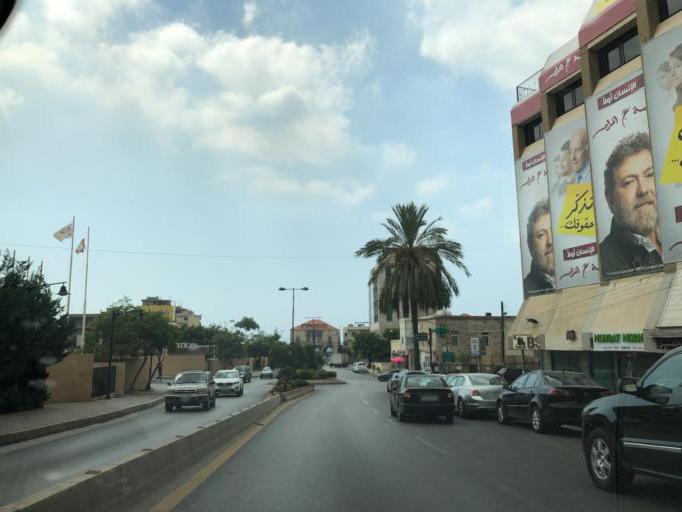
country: LB
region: Mont-Liban
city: Djounie
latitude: 33.9875
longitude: 35.6394
